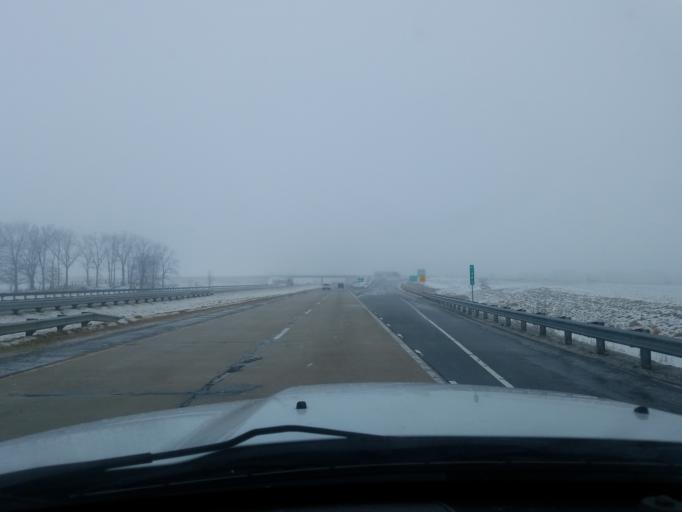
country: US
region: Indiana
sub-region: Tipton County
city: Tipton
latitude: 40.2713
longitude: -86.1269
